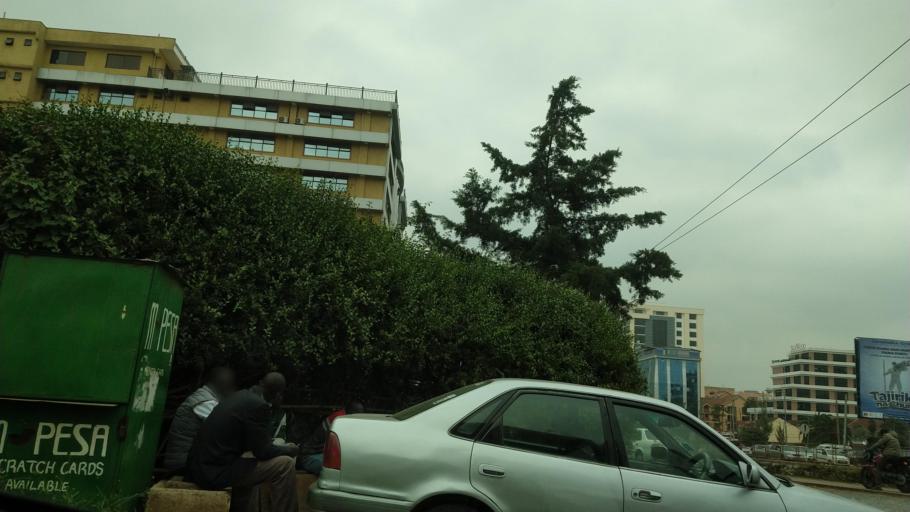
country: KE
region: Nairobi Area
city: Nairobi
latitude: -1.2996
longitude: 36.7821
